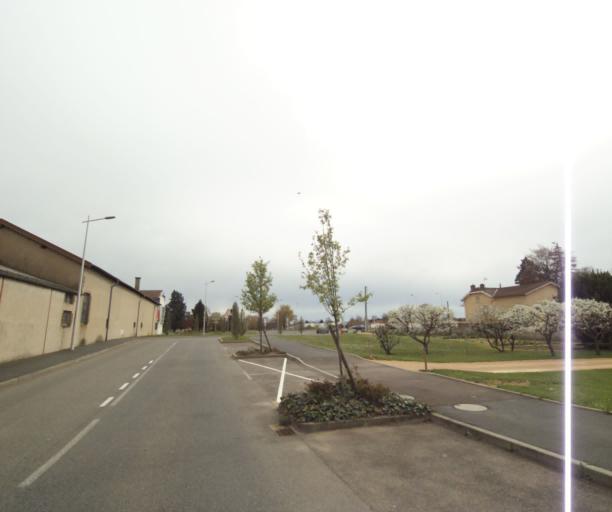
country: FR
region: Bourgogne
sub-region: Departement de Saone-et-Loire
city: Charnay-les-Macon
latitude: 46.3103
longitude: 4.8017
